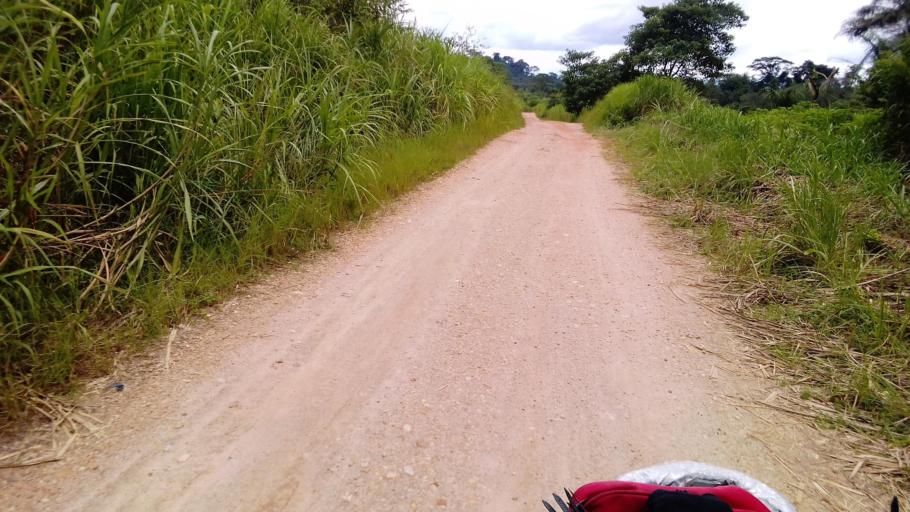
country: SL
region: Eastern Province
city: Koidu
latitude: 8.6813
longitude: -10.9654
